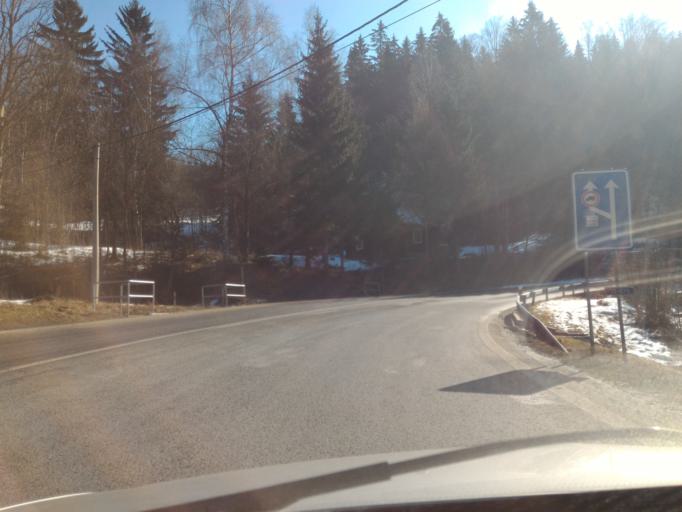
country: CZ
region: Liberecky
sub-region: Okres Jablonec nad Nisou
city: Korenov
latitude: 50.7631
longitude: 15.3474
